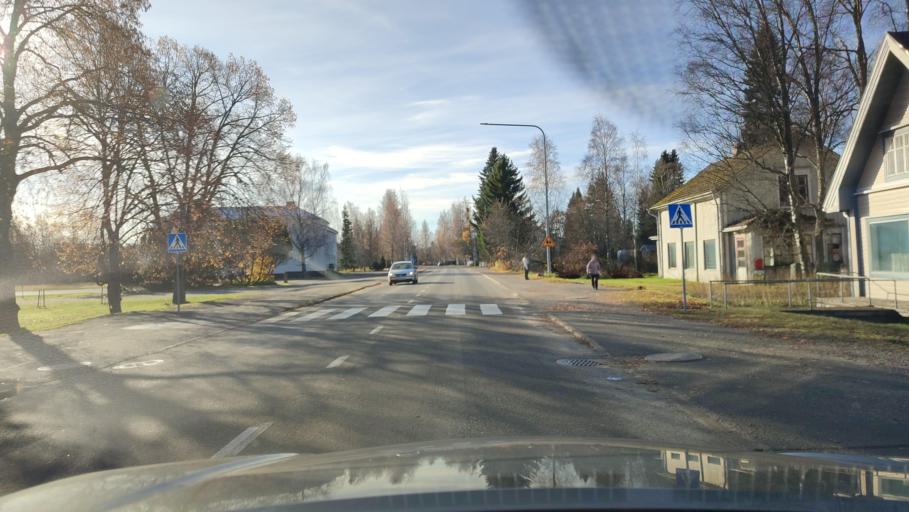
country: FI
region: Southern Ostrobothnia
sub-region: Suupohja
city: Teuva
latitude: 62.4849
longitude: 21.7457
